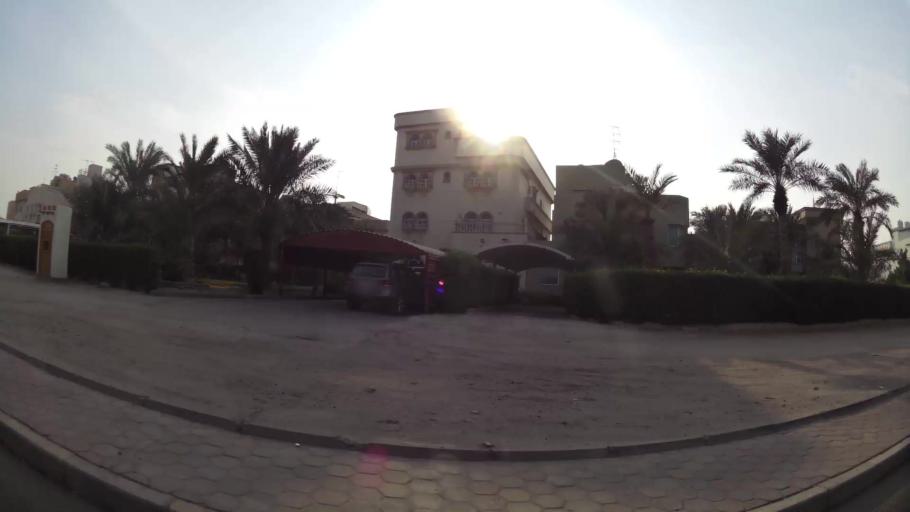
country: KW
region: Mubarak al Kabir
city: Mubarak al Kabir
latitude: 29.2141
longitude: 48.0653
